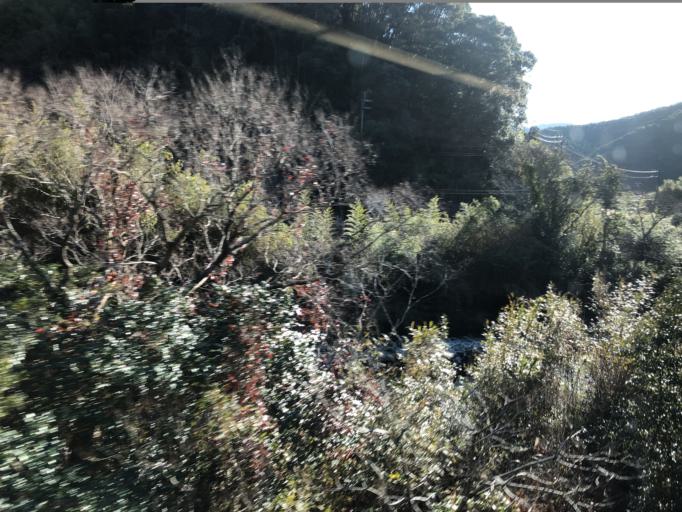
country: JP
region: Kochi
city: Nakamura
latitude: 33.1091
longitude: 133.1003
